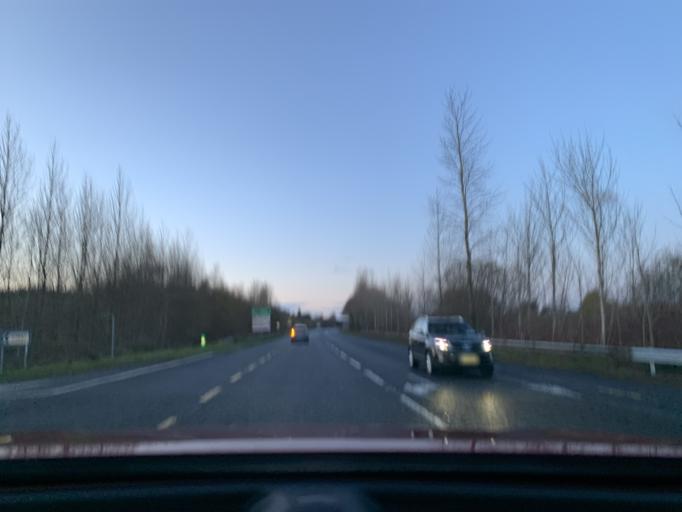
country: IE
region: Connaught
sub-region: County Leitrim
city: Carrick-on-Shannon
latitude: 53.9253
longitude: -7.9962
